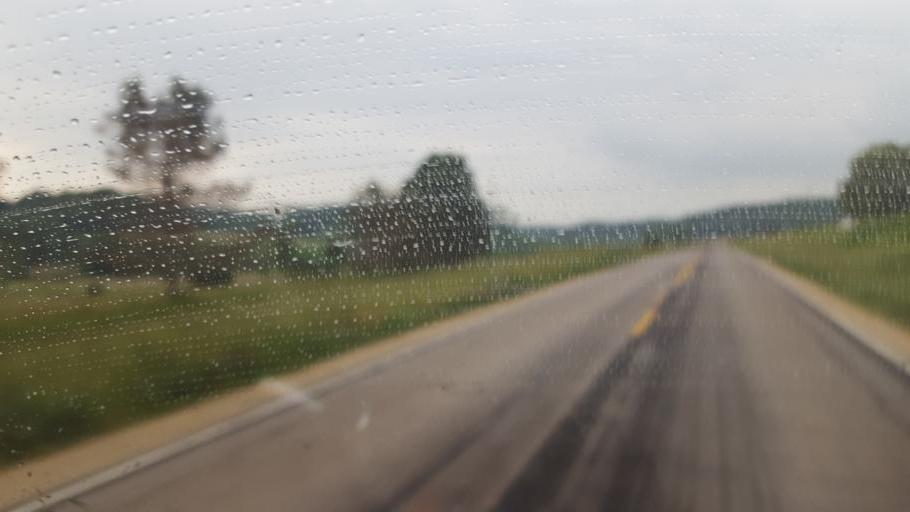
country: US
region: Wisconsin
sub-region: Vernon County
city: Hillsboro
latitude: 43.6456
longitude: -90.4083
